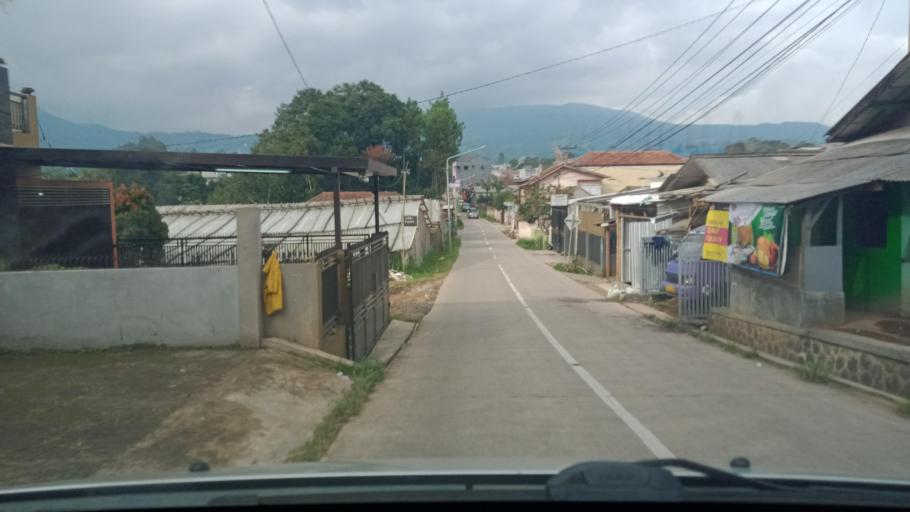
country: ID
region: West Java
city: Lembang
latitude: -6.8165
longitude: 107.5754
